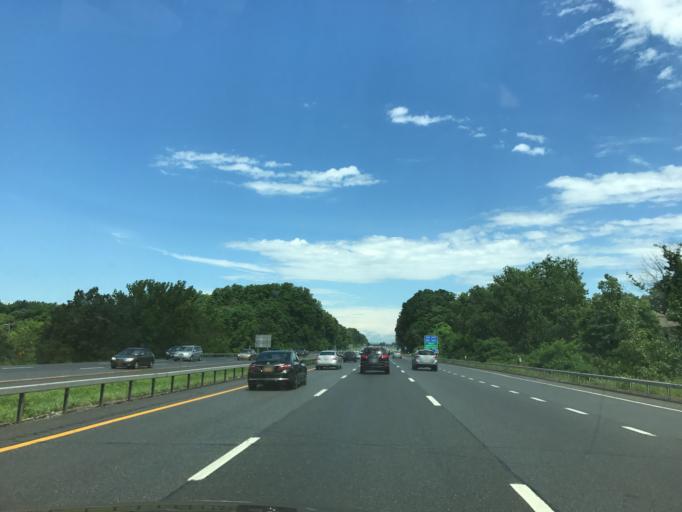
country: US
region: New York
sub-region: Saratoga County
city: Country Knolls
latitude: 42.8676
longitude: -73.7759
